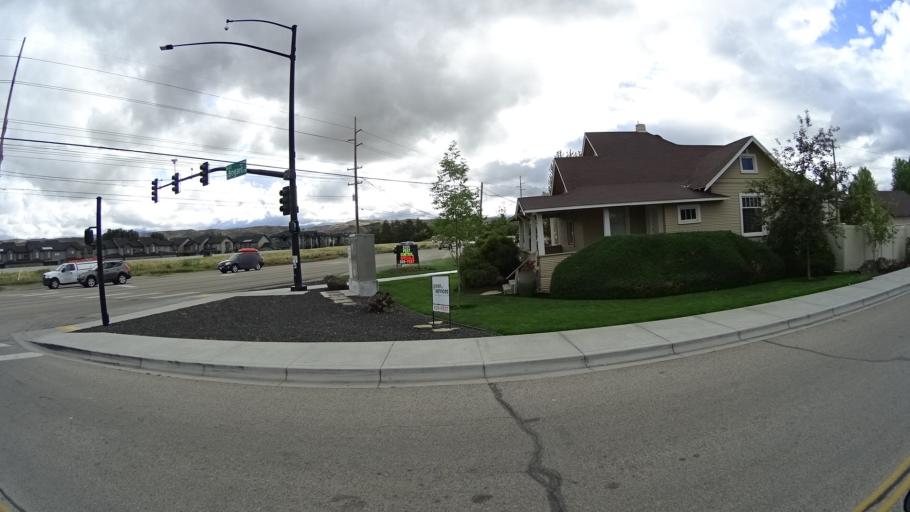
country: US
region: Idaho
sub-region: Ada County
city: Eagle
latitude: 43.6752
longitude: -116.2943
